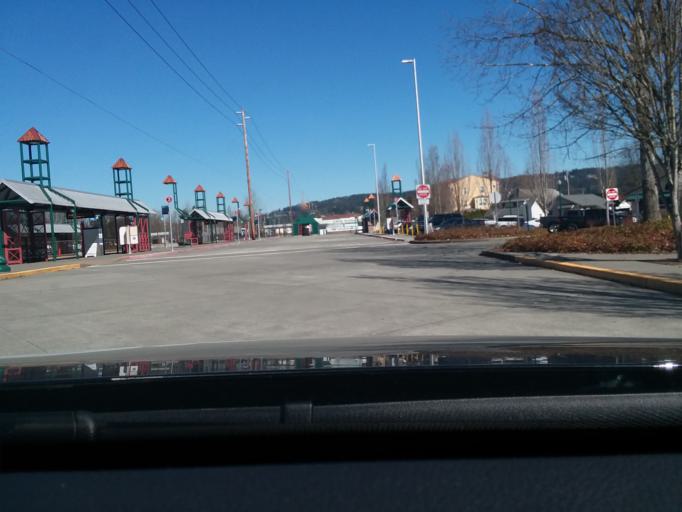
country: US
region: Washington
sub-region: Pierce County
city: Sumner
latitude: 47.2009
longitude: -122.2448
